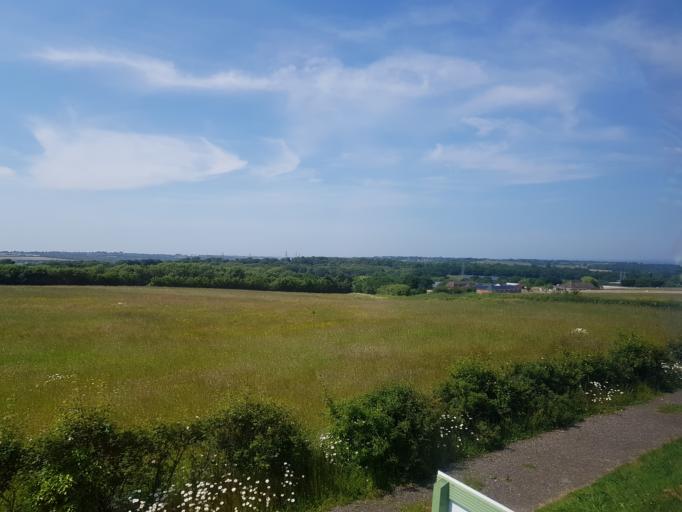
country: GB
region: England
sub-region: Isle of Wight
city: Newport
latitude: 50.7058
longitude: -1.2618
